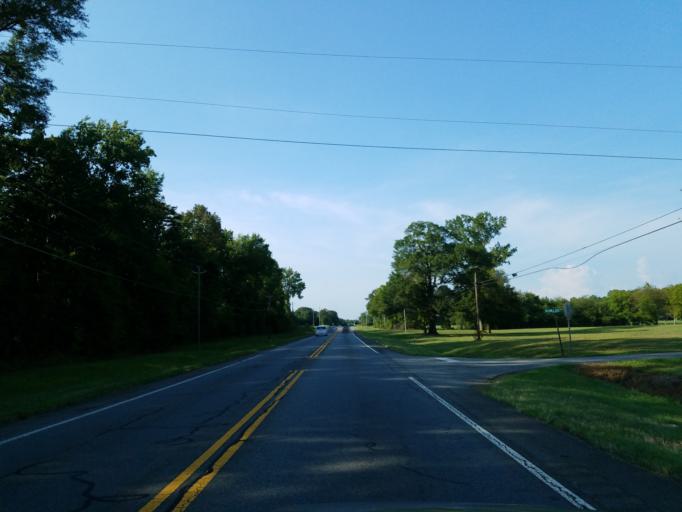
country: US
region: Georgia
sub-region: Bartow County
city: Rydal
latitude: 34.2998
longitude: -84.7316
